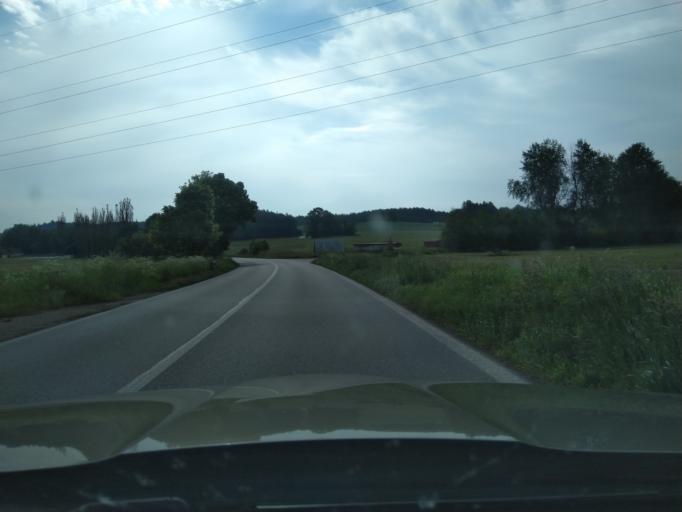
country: CZ
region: Jihocesky
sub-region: Okres Prachatice
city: Strunkovice nad Blanici
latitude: 49.0532
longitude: 14.0973
